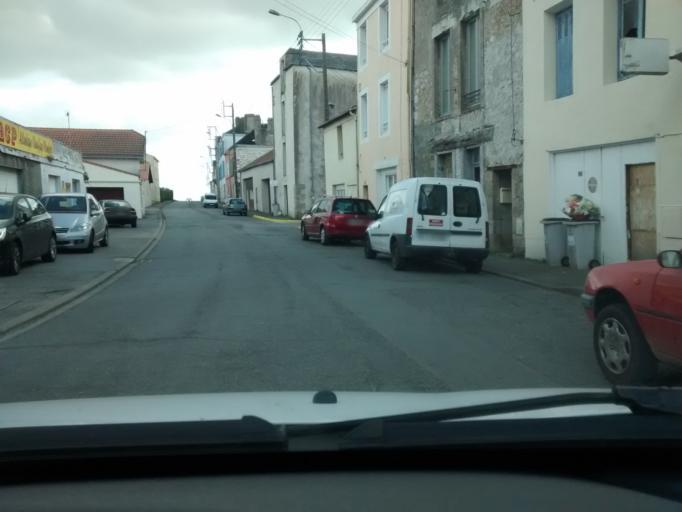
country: FR
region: Pays de la Loire
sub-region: Departement de la Loire-Atlantique
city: Saint-Paimboeuf
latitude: 47.2884
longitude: -2.0261
